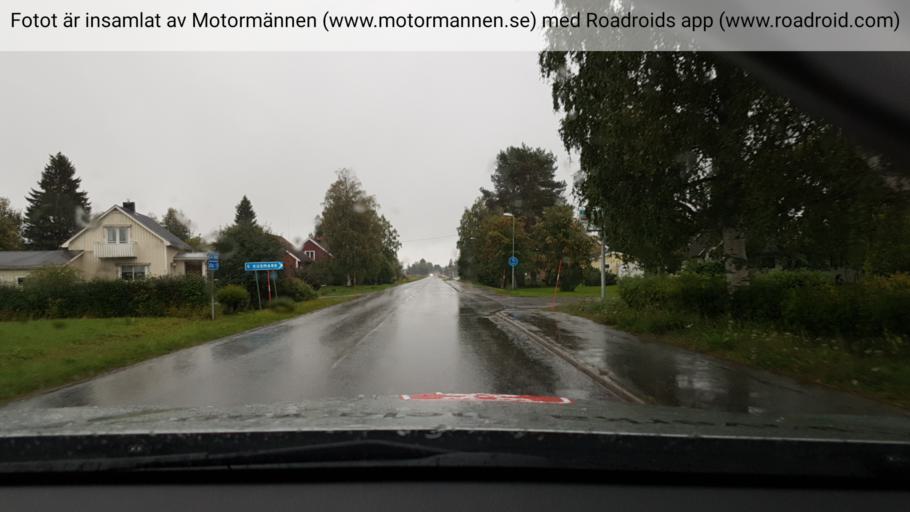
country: SE
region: Vaesterbotten
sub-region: Skelleftea Kommun
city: Kage
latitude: 64.8754
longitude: 20.8096
